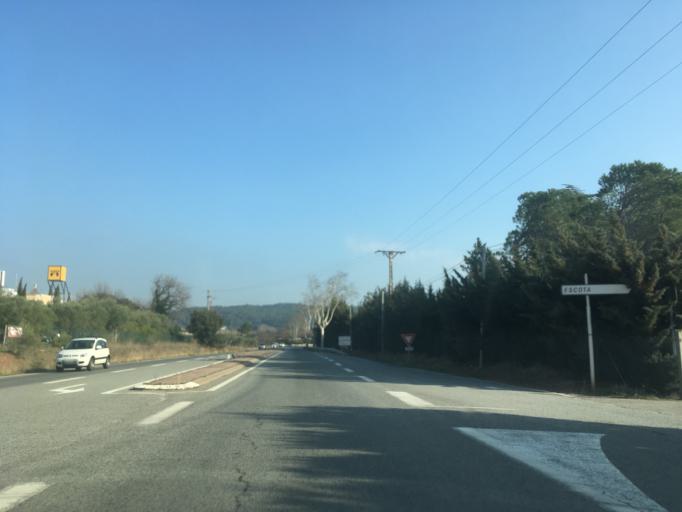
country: FR
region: Provence-Alpes-Cote d'Azur
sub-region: Departement du Var
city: Le Cannet-des-Maures
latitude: 43.3951
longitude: 6.3530
